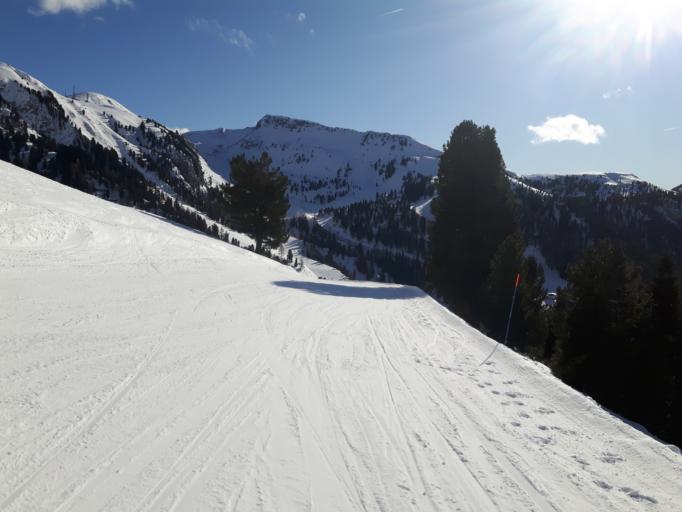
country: IT
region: Trentino-Alto Adige
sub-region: Provincia di Trento
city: Predazzo
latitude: 46.3486
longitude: 11.5498
